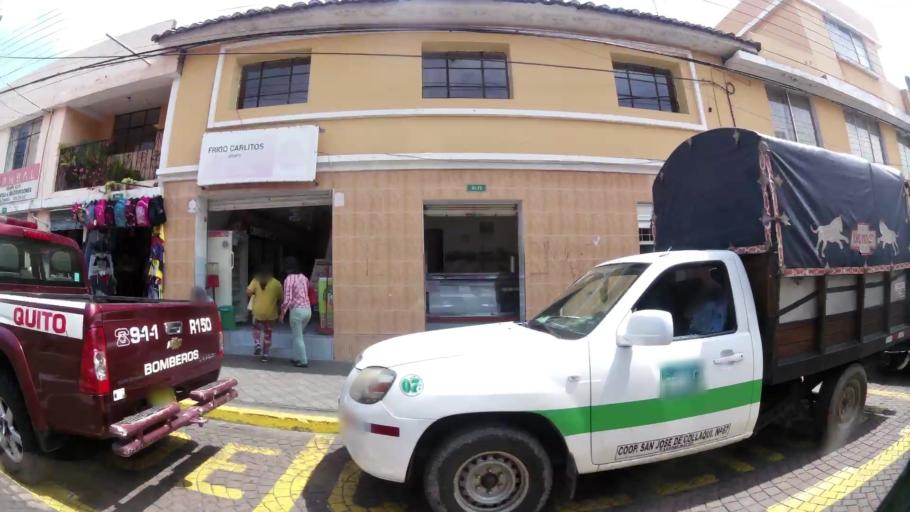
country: EC
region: Pichincha
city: Quito
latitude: -0.2131
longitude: -78.4055
